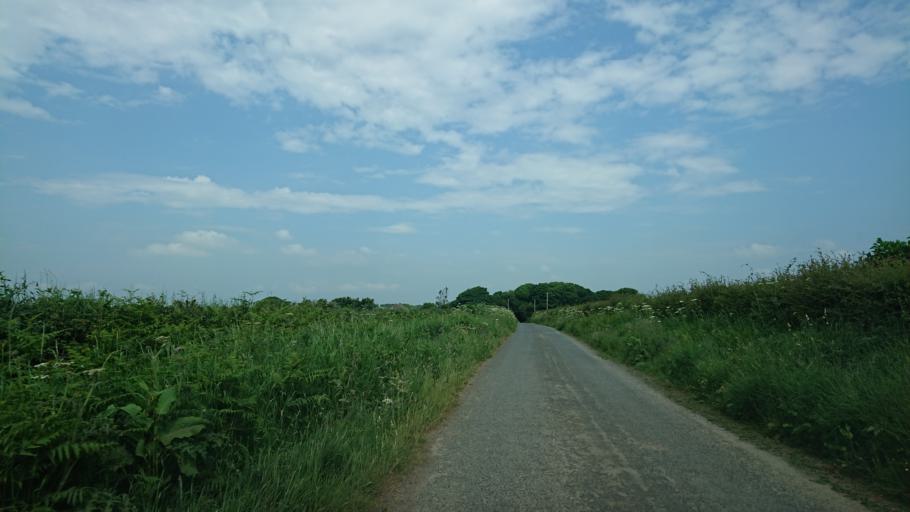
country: IE
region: Munster
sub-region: Waterford
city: Dunmore East
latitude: 52.2092
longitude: -6.9923
